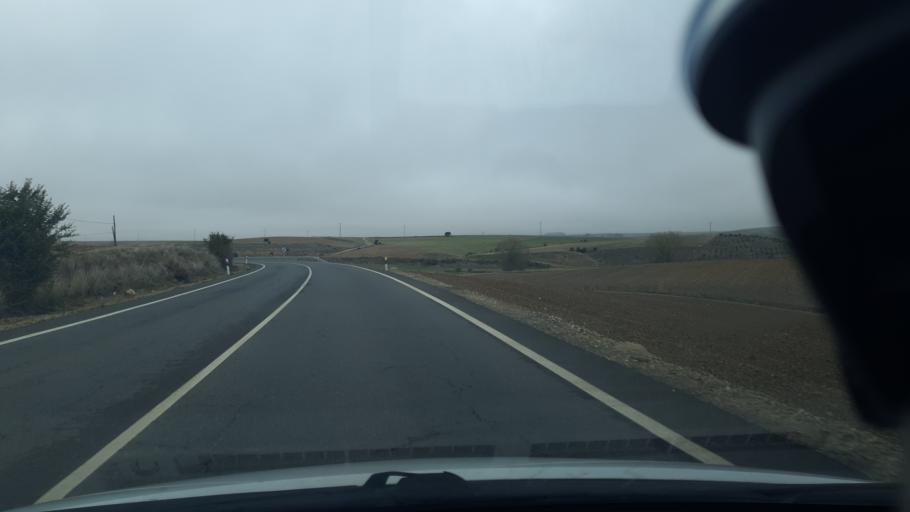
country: ES
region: Castille and Leon
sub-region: Provincia de Segovia
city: Encinillas
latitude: 41.0056
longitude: -4.1496
